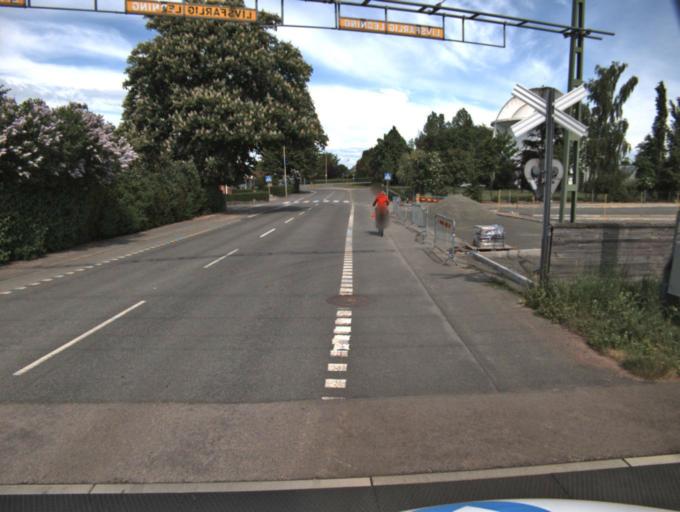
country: SE
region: Skane
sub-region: Kristianstads Kommun
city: Kristianstad
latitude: 56.0503
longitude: 14.1763
